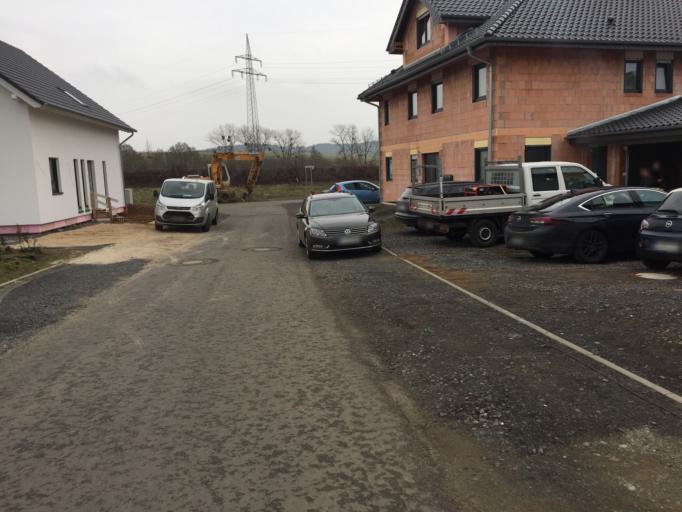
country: DE
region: Hesse
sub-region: Regierungsbezirk Giessen
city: Grunberg
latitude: 50.5783
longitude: 8.9559
